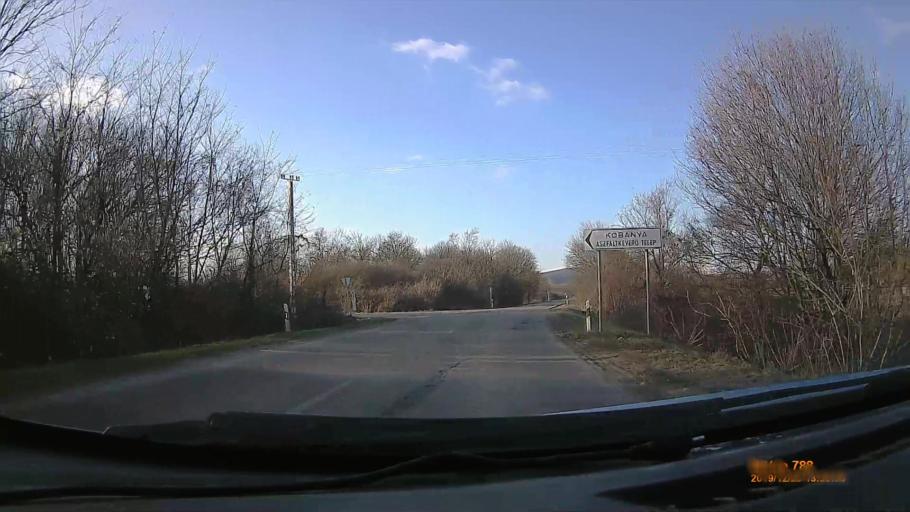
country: HU
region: Heves
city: Recsk
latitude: 47.9256
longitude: 20.1348
